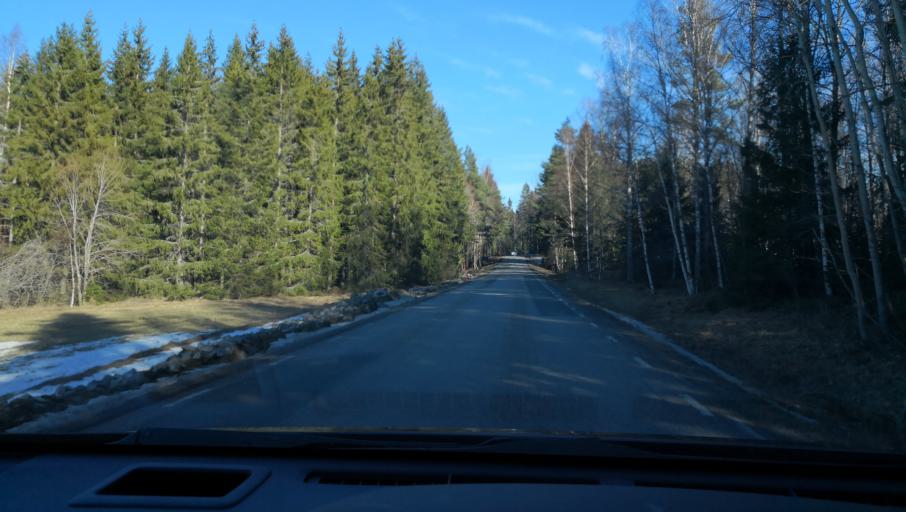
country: SE
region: Uppsala
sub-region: Osthammars Kommun
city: Osterbybruk
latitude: 60.2208
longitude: 17.9147
